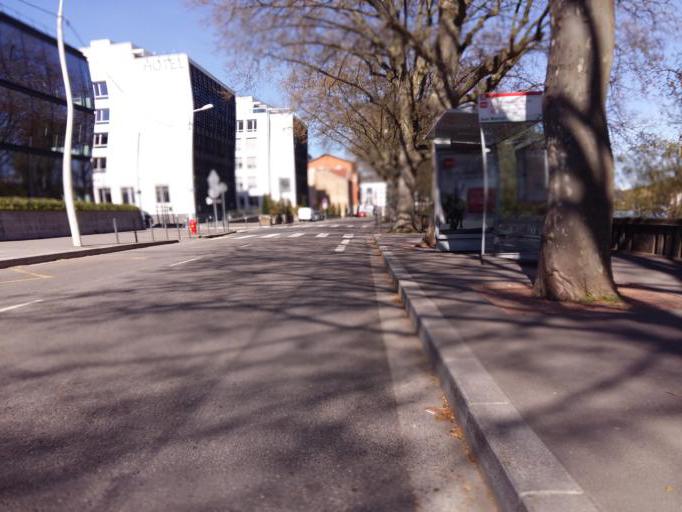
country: FR
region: Rhone-Alpes
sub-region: Departement du Rhone
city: Caluire-et-Cuire
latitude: 45.7876
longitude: 4.8148
